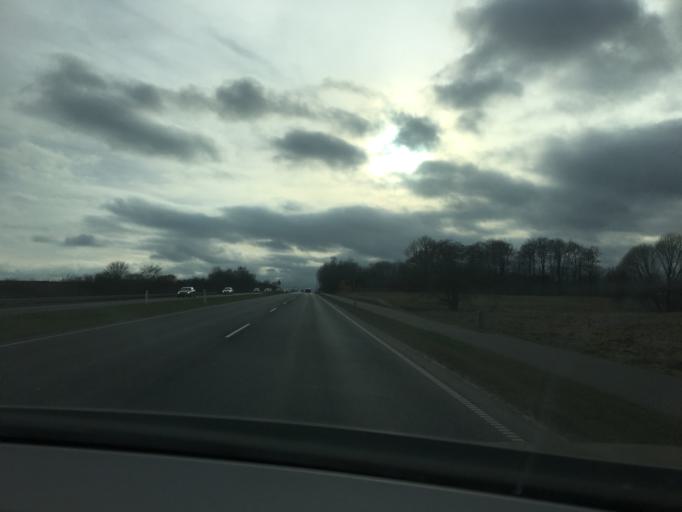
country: DK
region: South Denmark
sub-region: Vejle Kommune
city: Vejle
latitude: 55.7341
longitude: 9.6107
